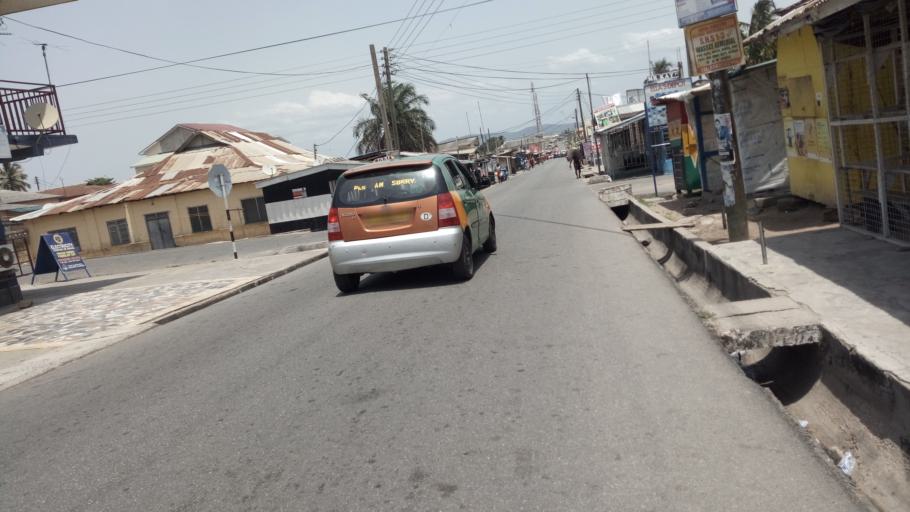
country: GH
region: Central
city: Winneba
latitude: 5.3455
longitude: -0.6238
